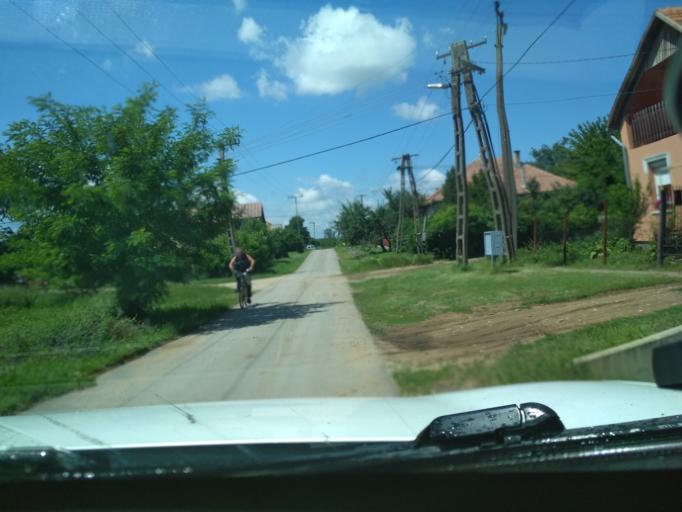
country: HU
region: Jasz-Nagykun-Szolnok
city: Abadszalok
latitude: 47.4812
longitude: 20.6134
